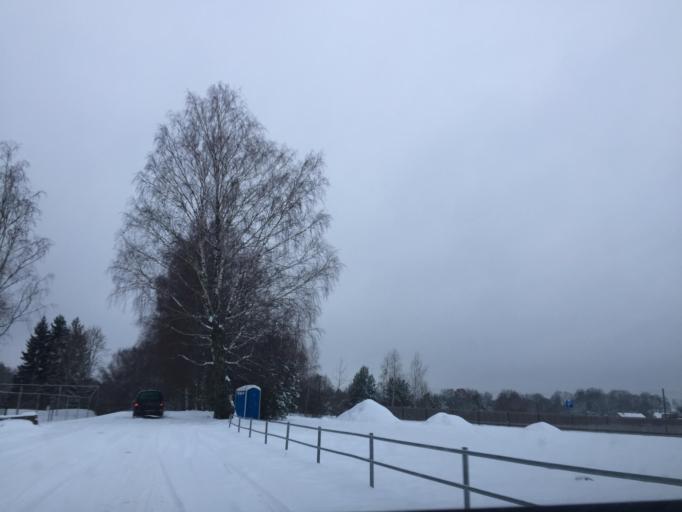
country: LV
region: Smiltene
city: Smiltene
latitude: 57.4310
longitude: 25.9197
